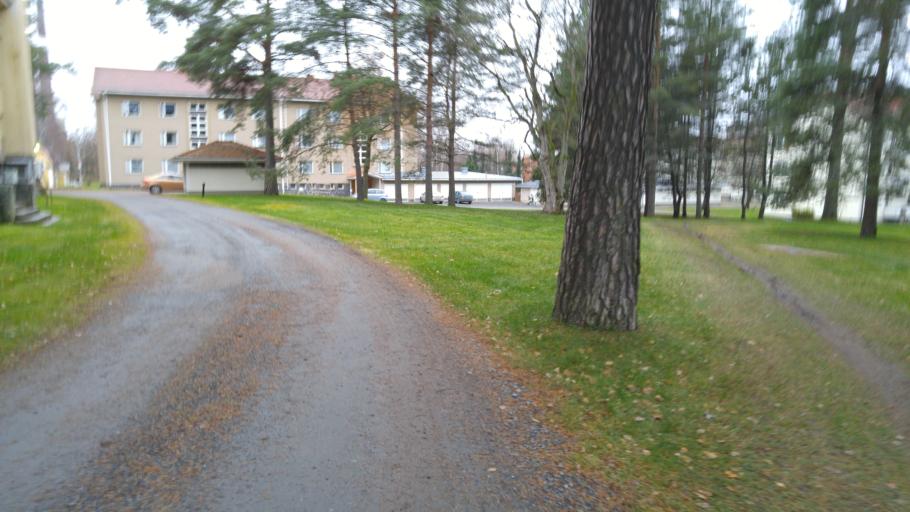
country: FI
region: Pirkanmaa
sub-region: Ylae-Pirkanmaa
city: Maenttae
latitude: 62.0278
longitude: 24.6450
